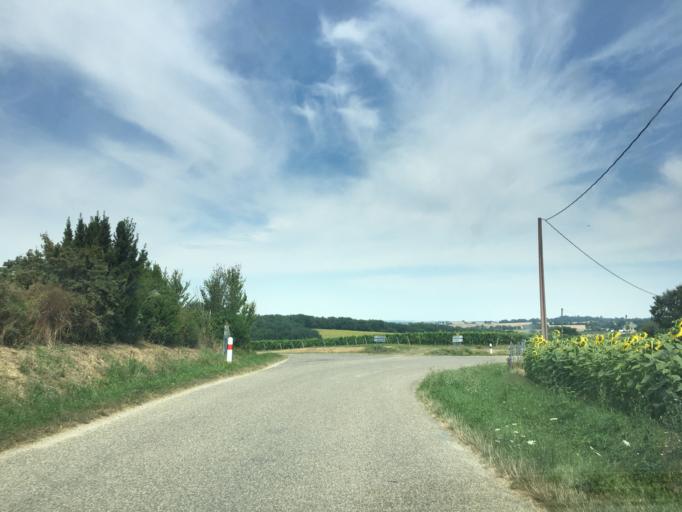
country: FR
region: Midi-Pyrenees
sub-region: Departement du Gers
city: Jegun
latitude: 43.8163
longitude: 0.5518
